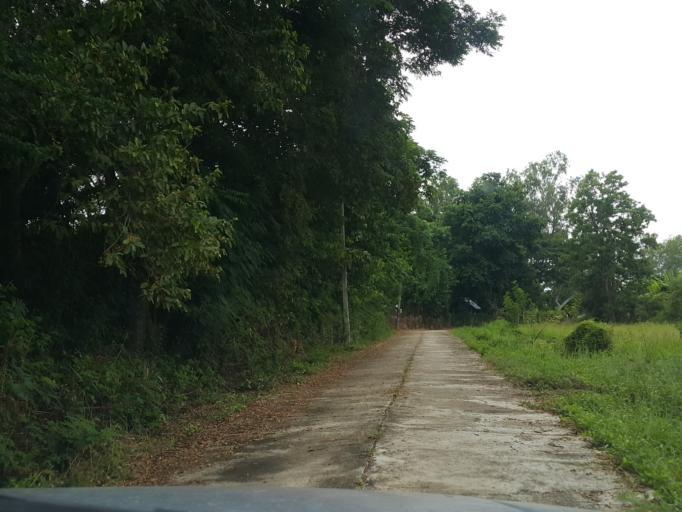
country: TH
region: Chiang Mai
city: San Kamphaeng
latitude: 18.8057
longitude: 99.1390
